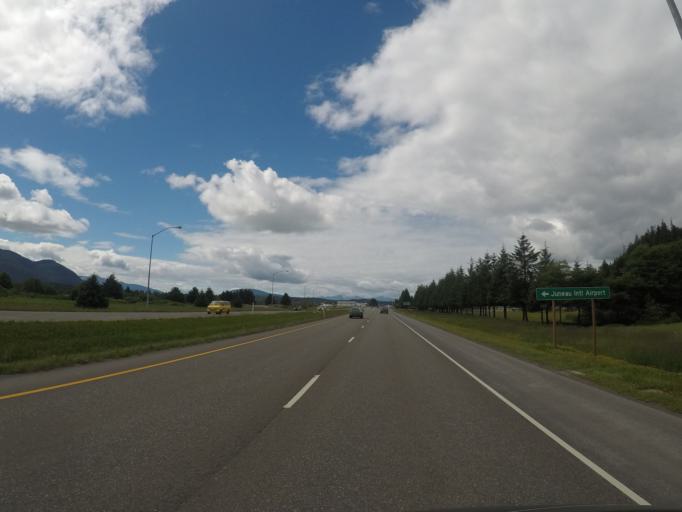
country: US
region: Alaska
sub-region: Juneau City and Borough
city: Juneau
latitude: 58.3584
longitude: -134.5522
